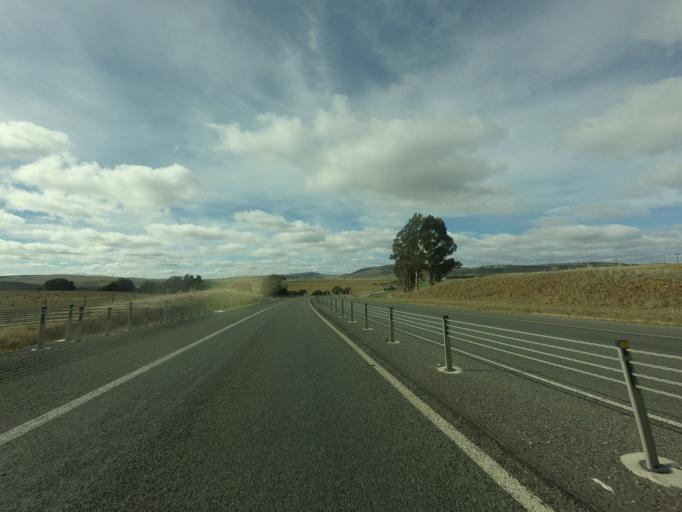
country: AU
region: Tasmania
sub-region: Brighton
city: Bridgewater
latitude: -42.3885
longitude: 147.2825
